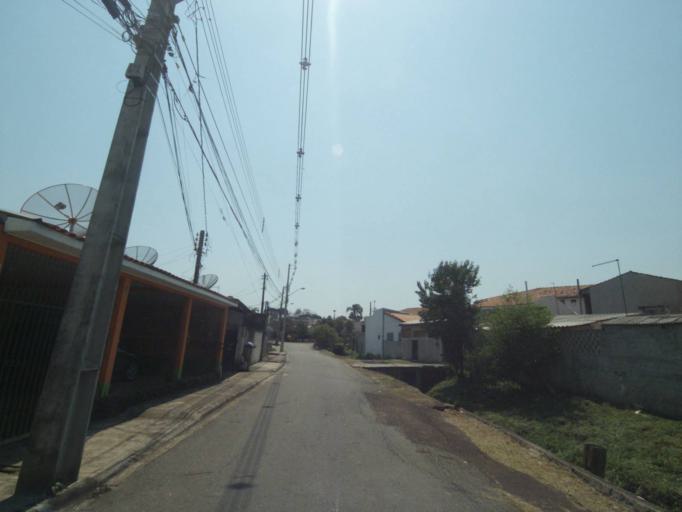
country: BR
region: Parana
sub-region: Sao Jose Dos Pinhais
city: Sao Jose dos Pinhais
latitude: -25.5059
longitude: -49.2686
